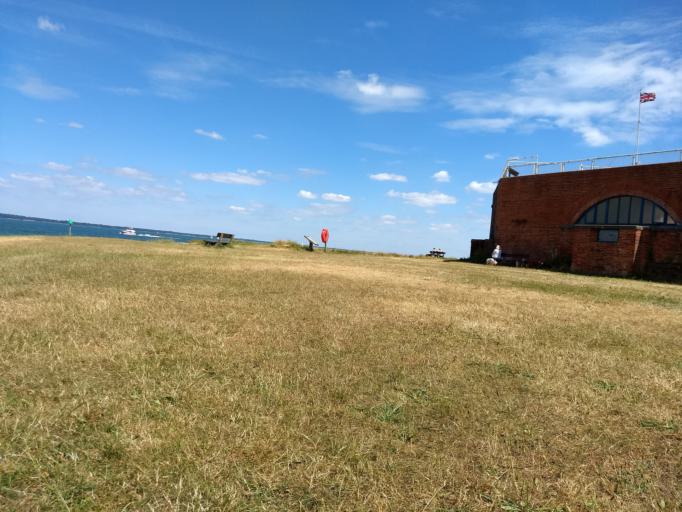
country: GB
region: England
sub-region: Isle of Wight
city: Freshwater
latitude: 50.7068
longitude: -1.5224
